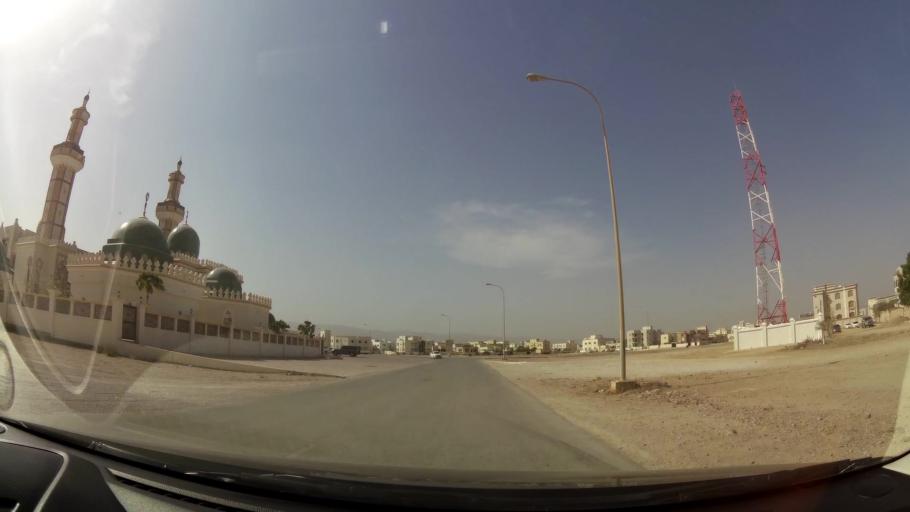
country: OM
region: Zufar
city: Salalah
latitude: 17.0004
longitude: 54.0134
